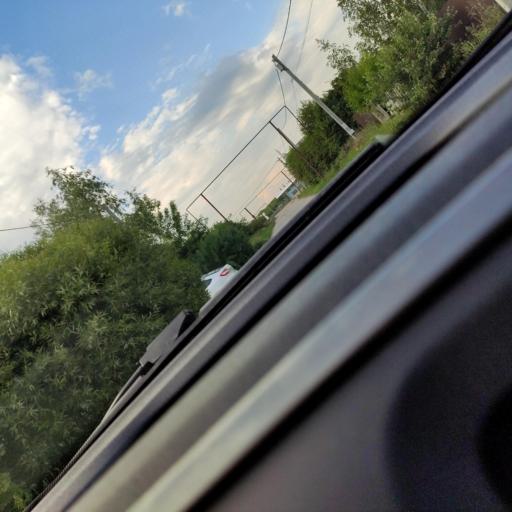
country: RU
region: Samara
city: Tol'yatti
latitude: 53.5698
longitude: 49.3871
